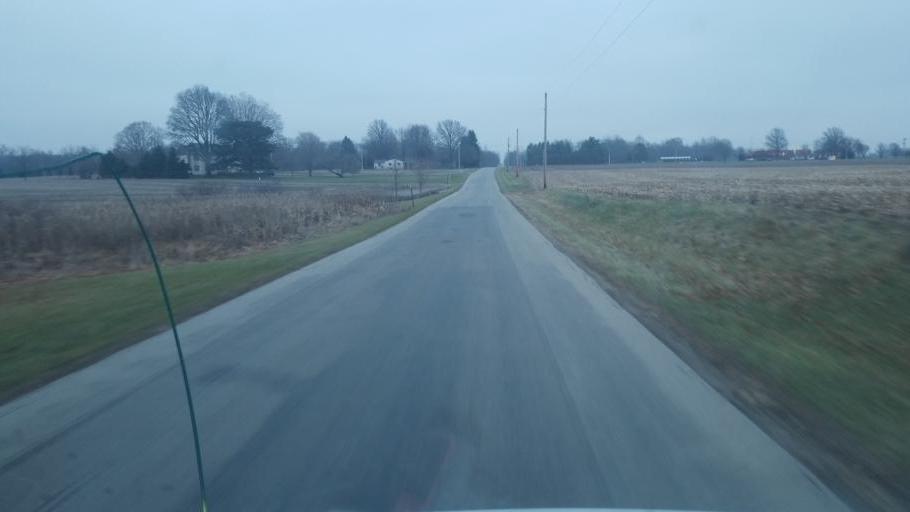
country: US
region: Ohio
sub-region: Seneca County
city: Tiffin
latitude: 40.9889
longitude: -83.1752
